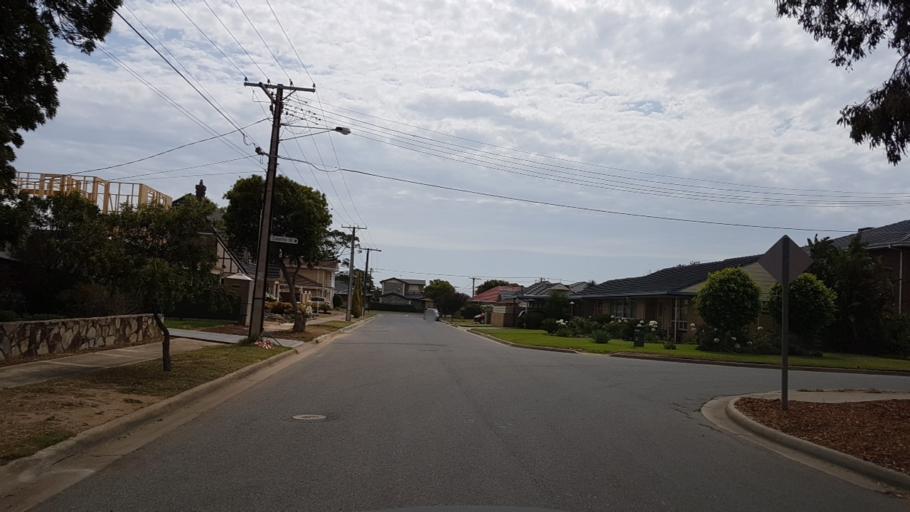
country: AU
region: South Australia
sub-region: Charles Sturt
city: Seaton
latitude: -34.9101
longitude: 138.5105
